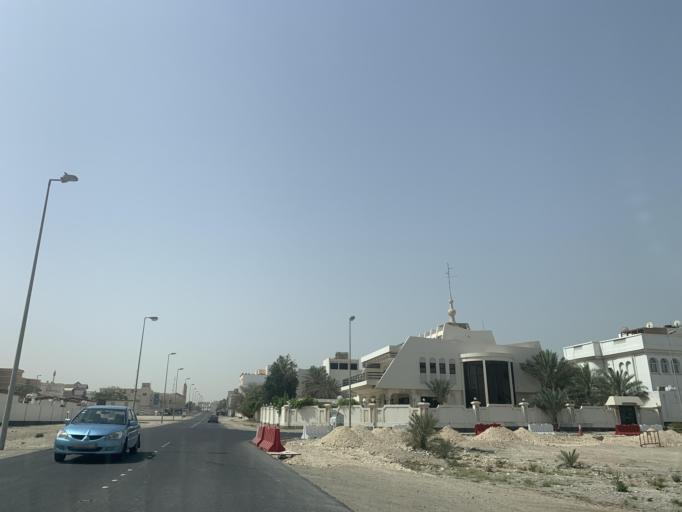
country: BH
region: Northern
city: Madinat `Isa
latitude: 26.1524
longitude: 50.5288
